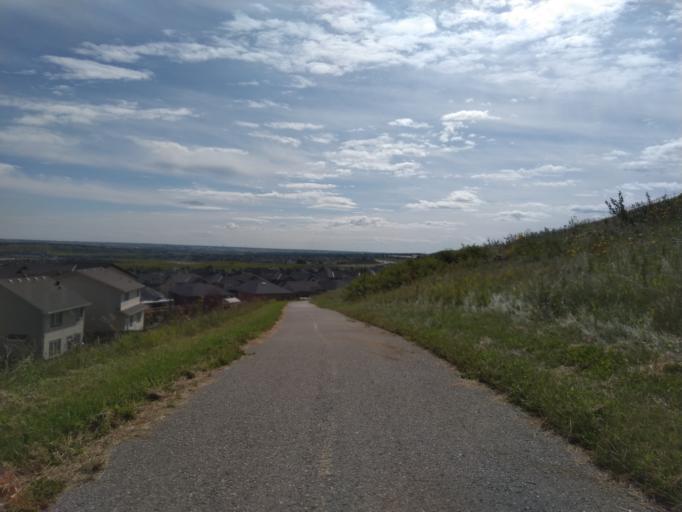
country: CA
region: Alberta
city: Calgary
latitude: 51.1572
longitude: -114.1547
